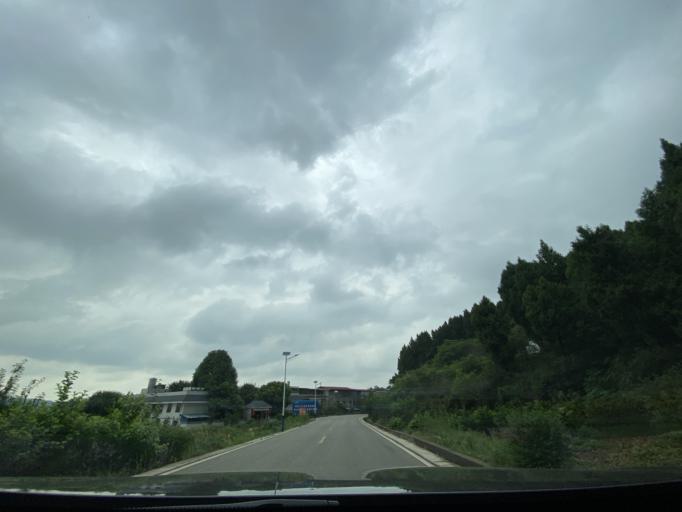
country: CN
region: Sichuan
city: Jiancheng
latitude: 30.5396
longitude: 104.5217
